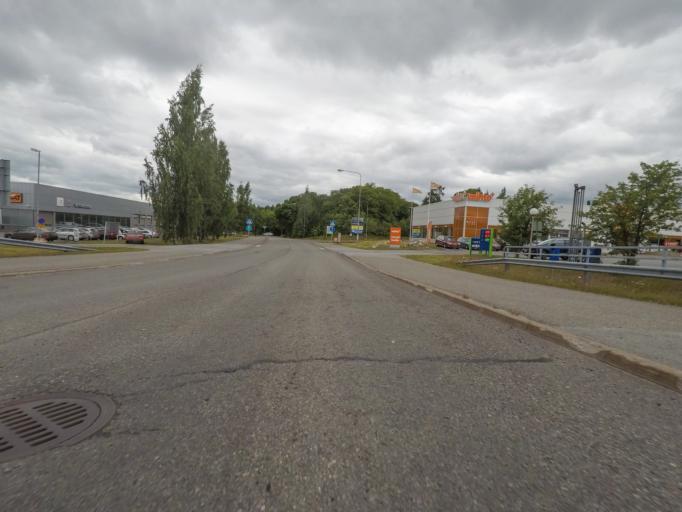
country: FI
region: Varsinais-Suomi
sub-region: Turku
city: Raisio
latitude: 60.4914
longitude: 22.1895
